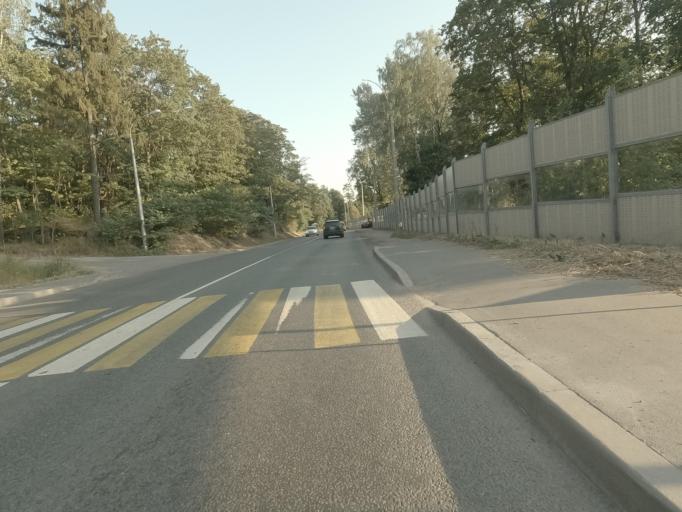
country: RU
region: Leningrad
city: Vyborg
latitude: 60.7229
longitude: 28.7683
